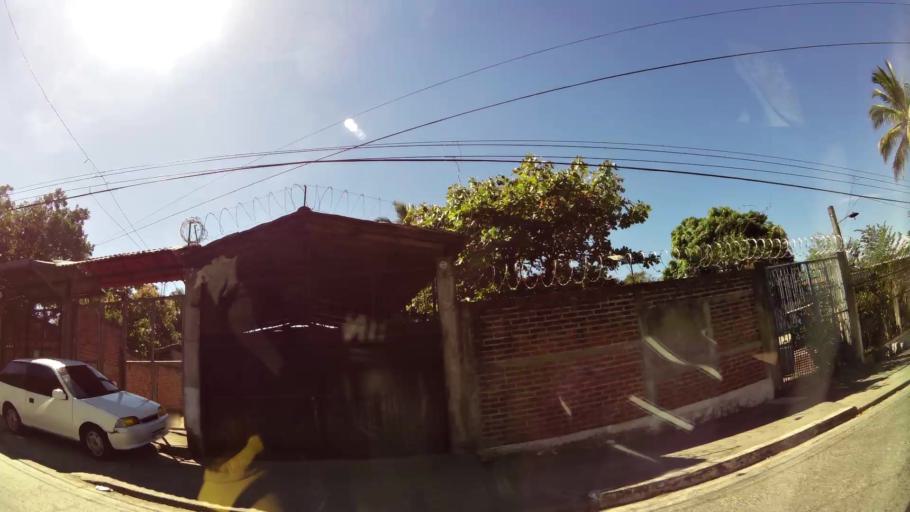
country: SV
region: La Libertad
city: San Juan Opico
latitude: 13.8774
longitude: -89.3547
